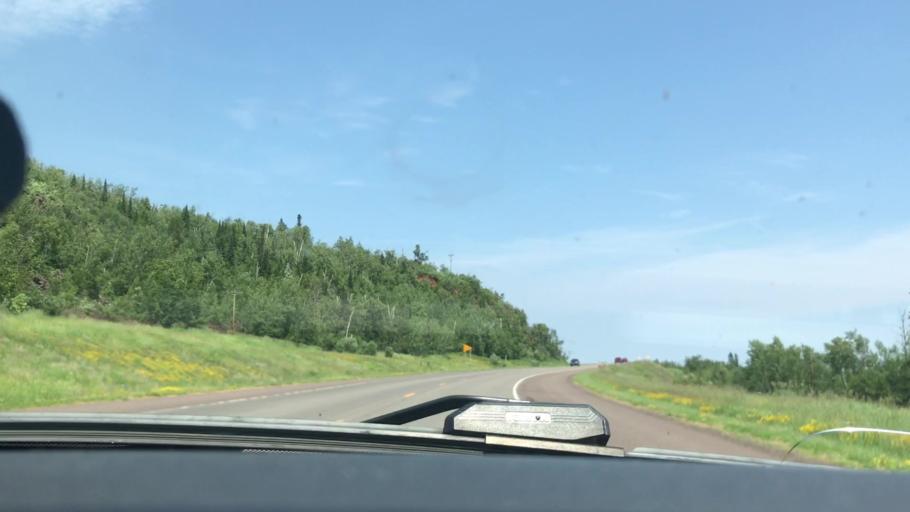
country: US
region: Minnesota
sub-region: Lake County
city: Silver Bay
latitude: 47.3032
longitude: -91.2490
